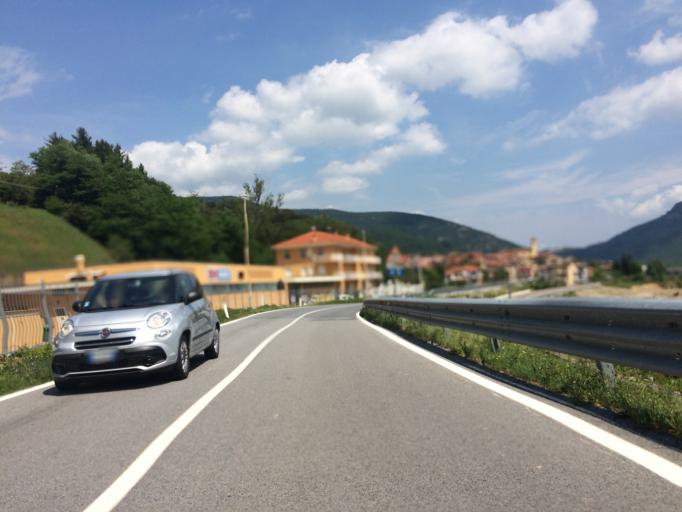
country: IT
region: Piedmont
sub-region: Provincia di Cuneo
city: Priola
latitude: 44.2551
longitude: 8.0200
